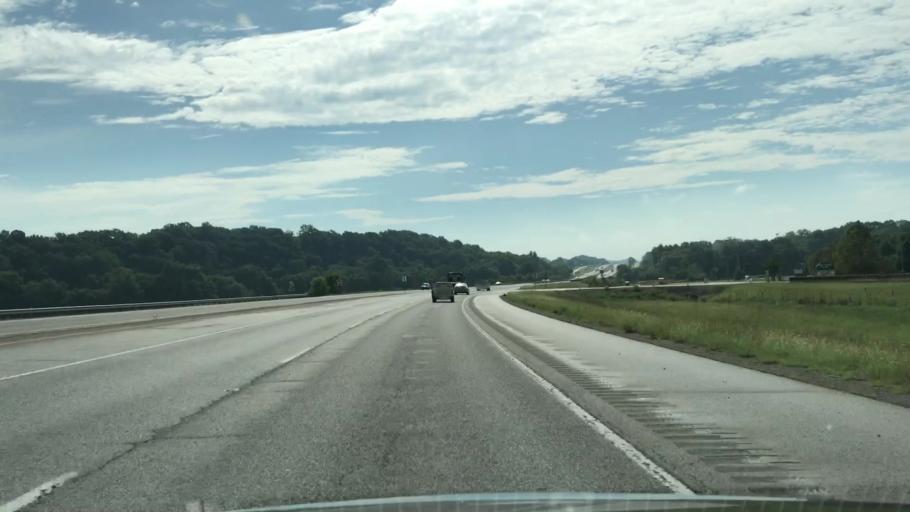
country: US
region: Kentucky
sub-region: Warren County
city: Plano
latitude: 36.8998
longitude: -86.3871
